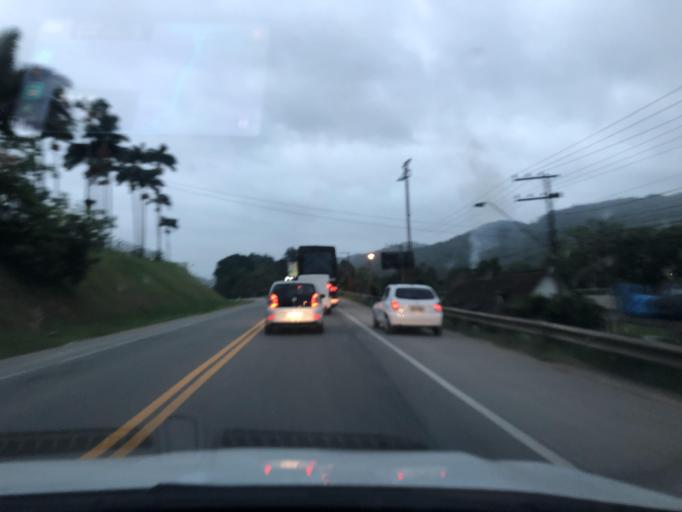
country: BR
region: Santa Catarina
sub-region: Pomerode
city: Pomerode
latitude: -26.7860
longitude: -49.0855
